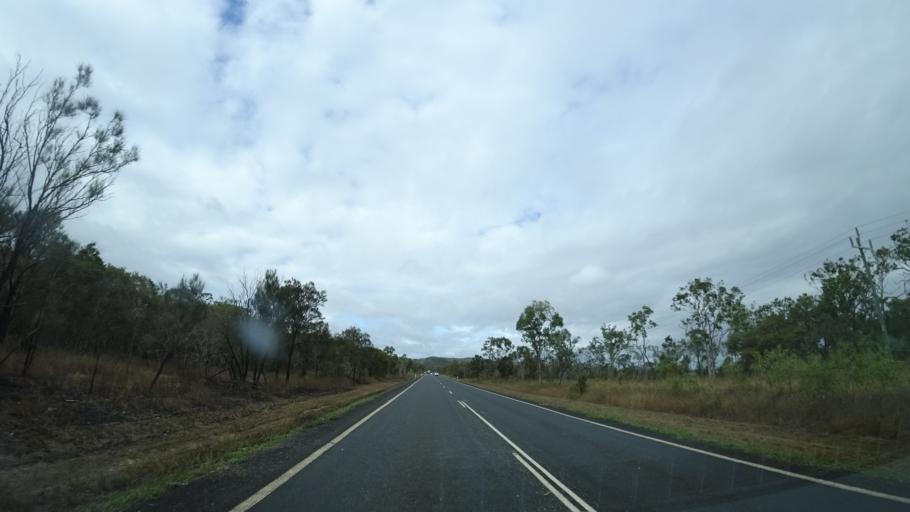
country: AU
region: Queensland
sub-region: Tablelands
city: Mareeba
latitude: -16.7813
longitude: 145.3441
